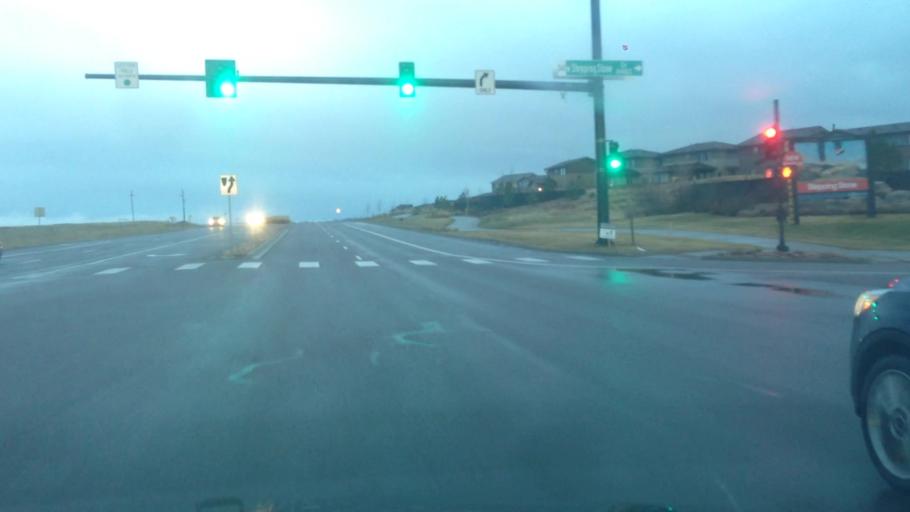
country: US
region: Colorado
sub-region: Douglas County
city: Stonegate
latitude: 39.5188
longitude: -104.8224
